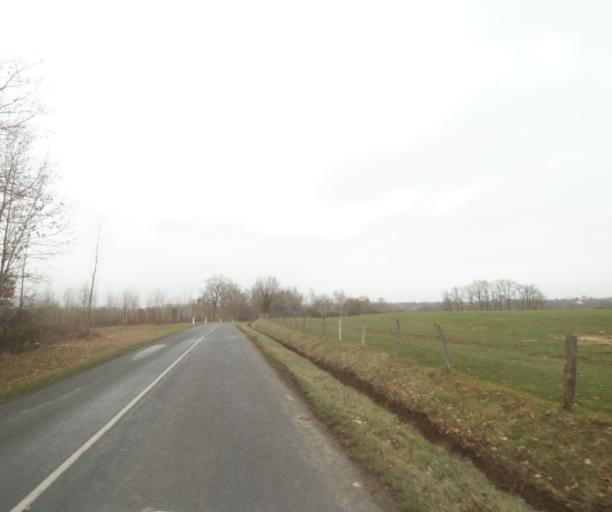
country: FR
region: Champagne-Ardenne
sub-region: Departement de la Marne
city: Pargny-sur-Saulx
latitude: 48.7394
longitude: 4.8546
